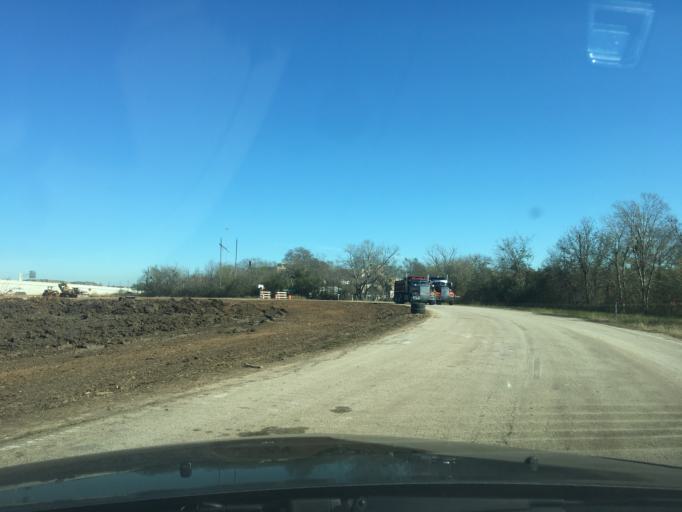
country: US
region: Texas
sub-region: Fort Bend County
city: Greatwood
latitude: 29.5540
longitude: -95.7173
